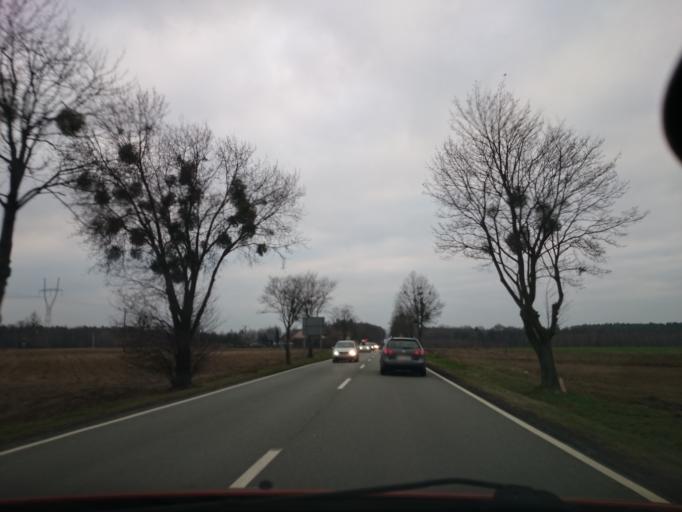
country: PL
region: Opole Voivodeship
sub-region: Powiat opolski
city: Niemodlin
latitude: 50.6198
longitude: 17.5734
